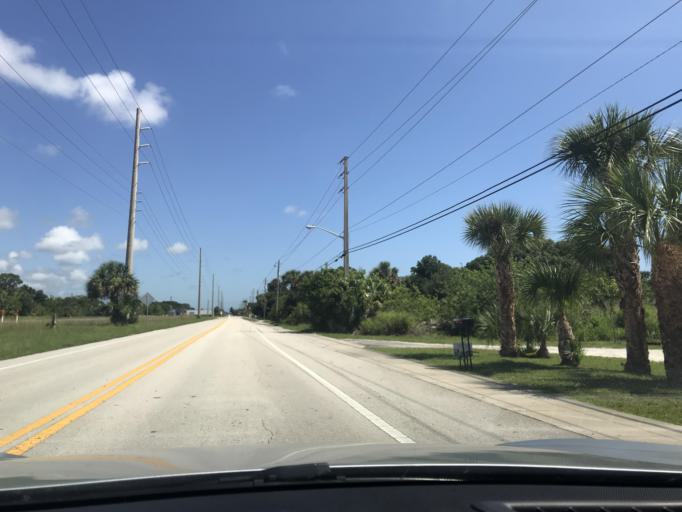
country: US
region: Florida
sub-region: Indian River County
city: Gifford
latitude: 27.6700
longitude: -80.4076
